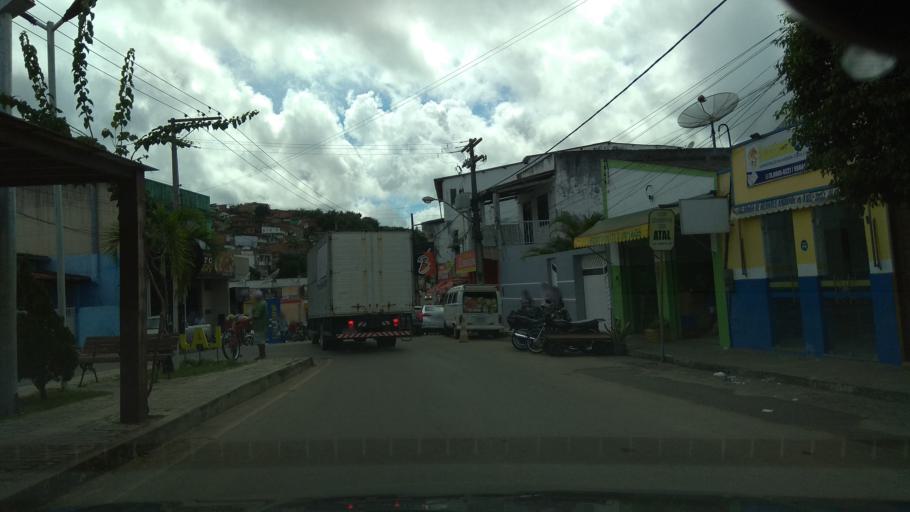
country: BR
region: Bahia
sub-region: Mutuipe
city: Mutuipe
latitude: -13.1831
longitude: -39.4224
